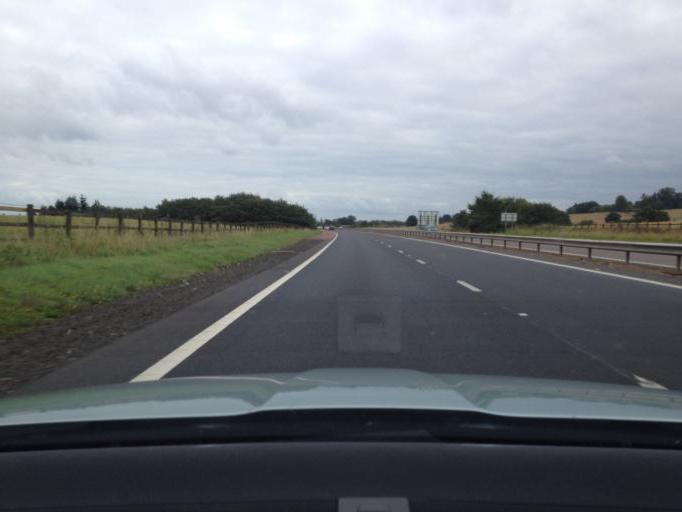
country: GB
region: Scotland
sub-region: Fife
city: Kelty
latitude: 56.1563
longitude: -3.3989
